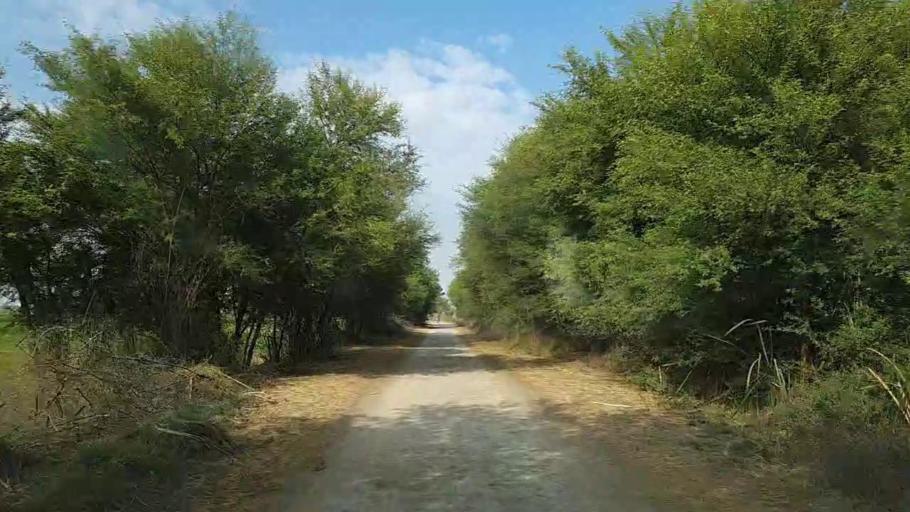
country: PK
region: Sindh
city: Sanghar
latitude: 26.2479
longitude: 69.0139
